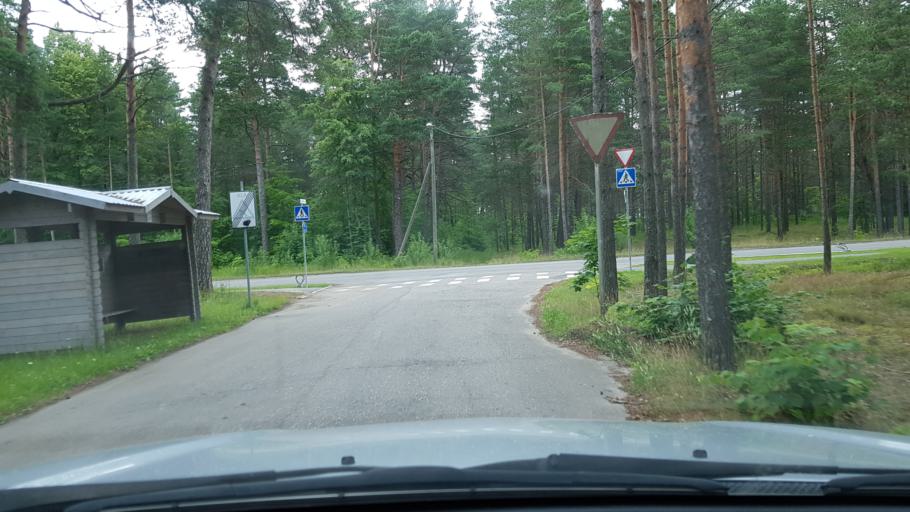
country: EE
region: Ida-Virumaa
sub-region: Narva-Joesuu linn
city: Narva-Joesuu
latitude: 59.4558
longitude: 28.0618
